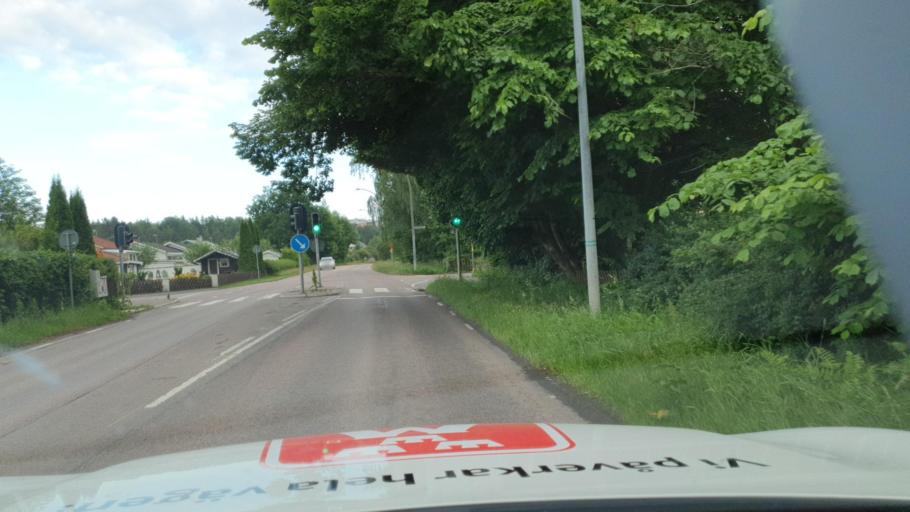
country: SE
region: Vaermland
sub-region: Karlstads Kommun
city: Karlstad
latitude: 59.4028
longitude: 13.5124
